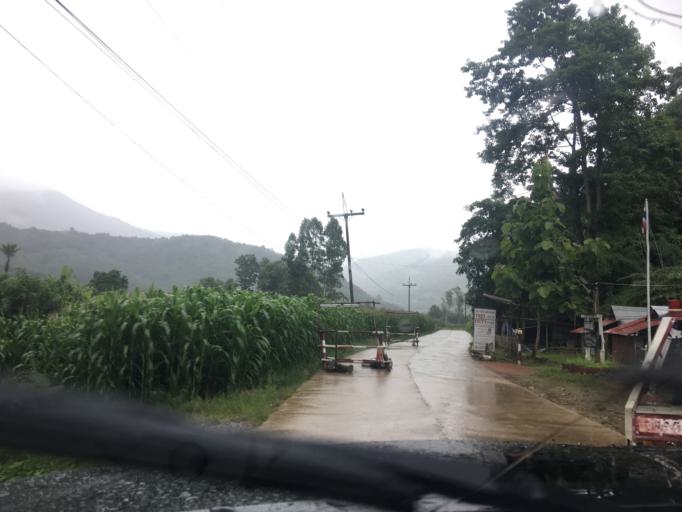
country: TH
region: Chiang Rai
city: Chiang Khong
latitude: 20.2987
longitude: 100.2562
